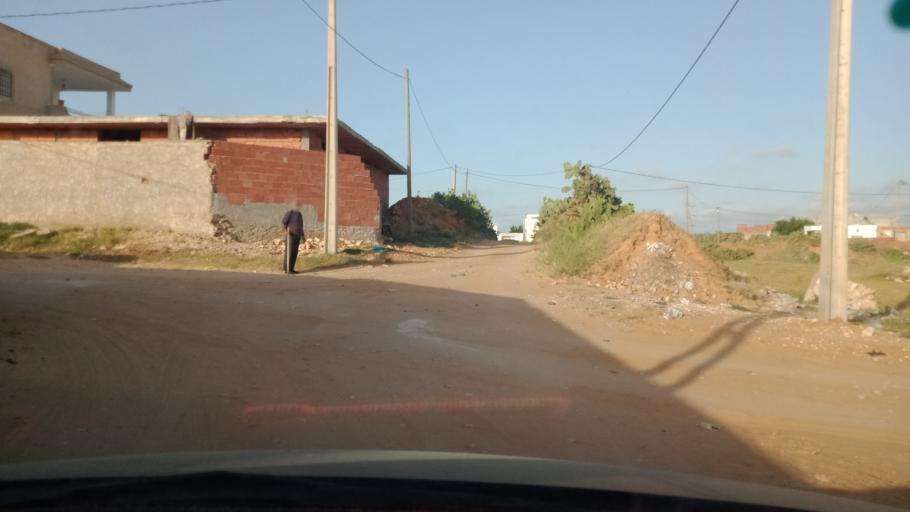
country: TN
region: Safaqis
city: Al Qarmadah
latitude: 34.8213
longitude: 10.7470
